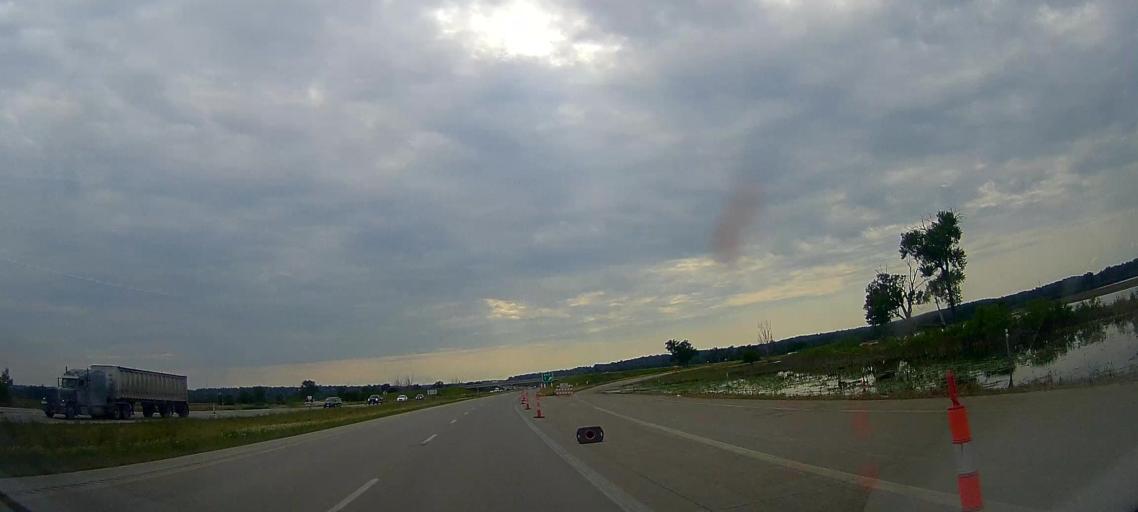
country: US
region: Iowa
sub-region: Pottawattamie County
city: Carter Lake
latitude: 41.3464
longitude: -95.9297
